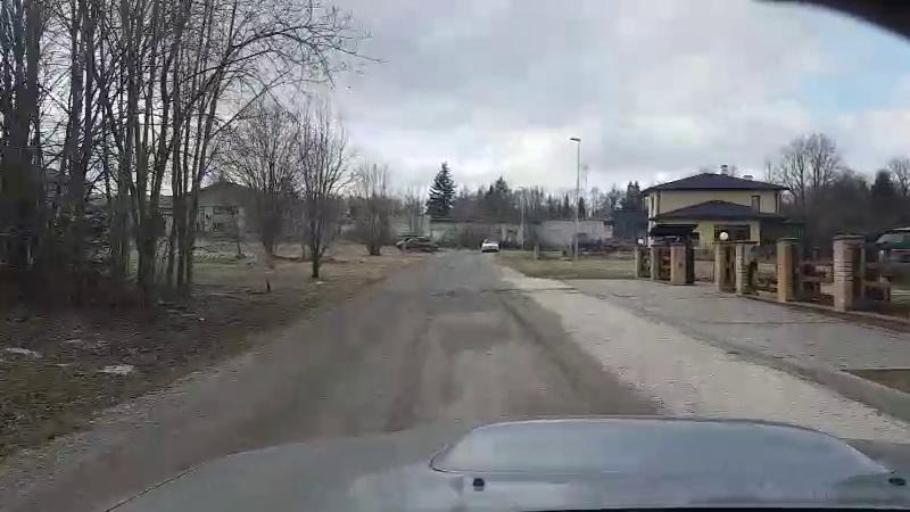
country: EE
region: Jaervamaa
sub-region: Paide linn
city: Paide
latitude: 58.8798
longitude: 25.5382
